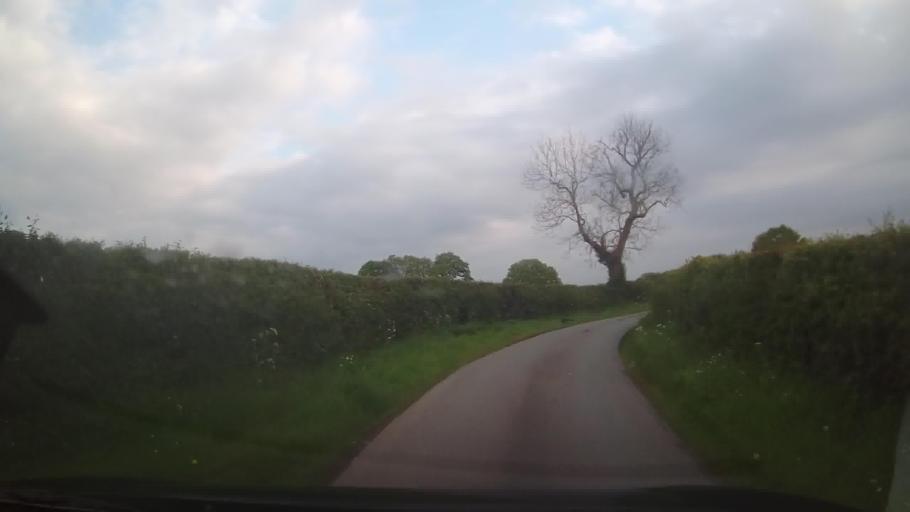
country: GB
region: England
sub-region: Shropshire
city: Ellesmere
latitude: 52.9405
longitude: -2.8637
